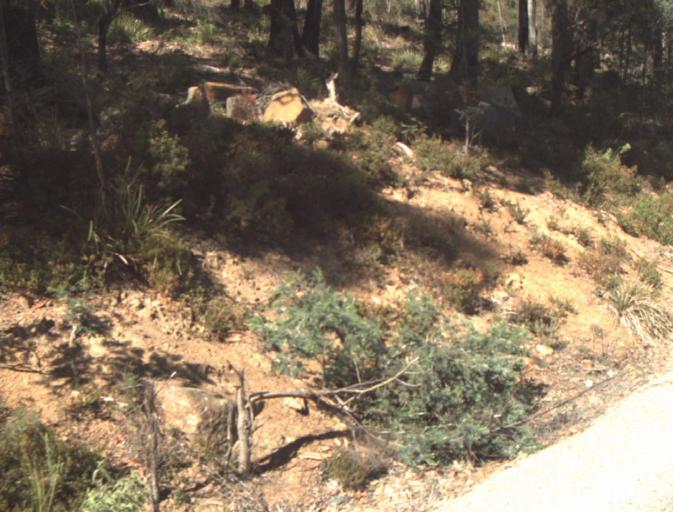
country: AU
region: Tasmania
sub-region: Launceston
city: Mayfield
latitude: -41.3360
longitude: 147.1979
